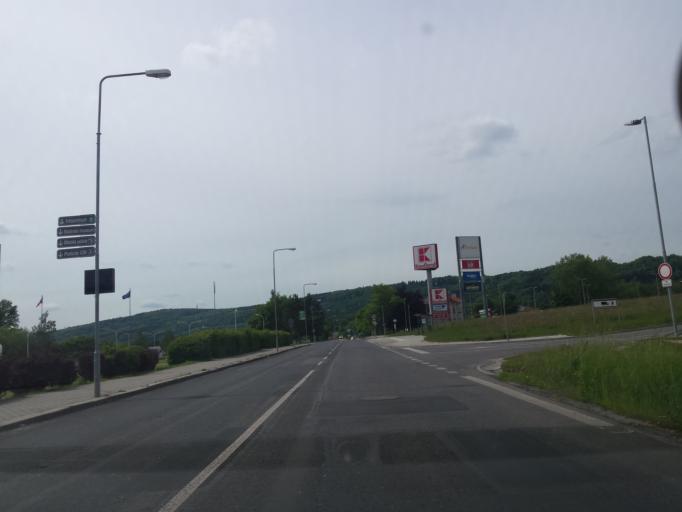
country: CZ
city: Novy Bor
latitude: 50.7645
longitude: 14.5454
